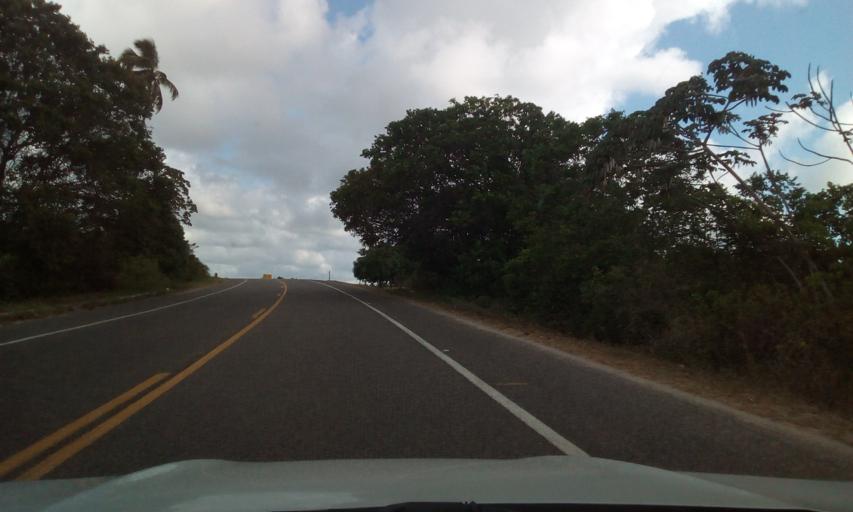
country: BR
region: Bahia
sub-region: Conde
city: Conde
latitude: -11.7989
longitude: -37.6272
